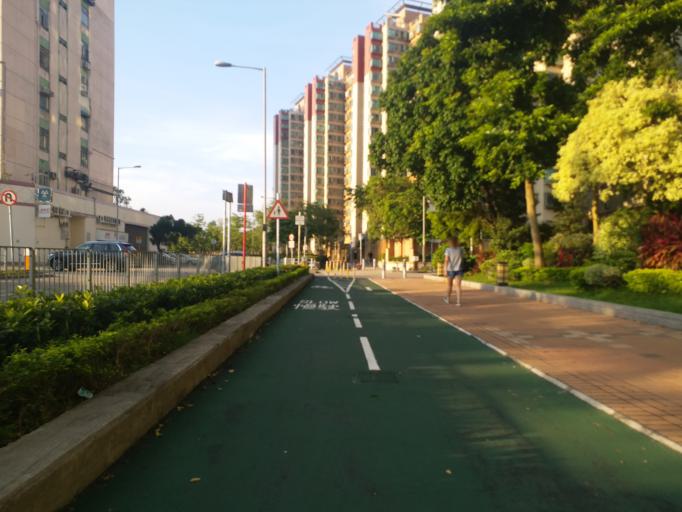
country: HK
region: Yuen Long
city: Yuen Long Kau Hui
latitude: 22.4497
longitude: 114.0314
